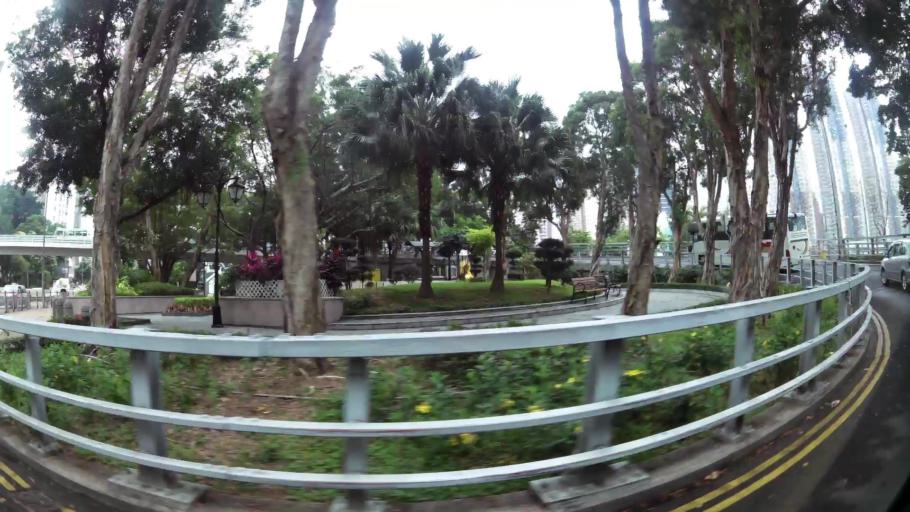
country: HK
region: Central and Western
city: Central
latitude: 22.2471
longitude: 114.1549
